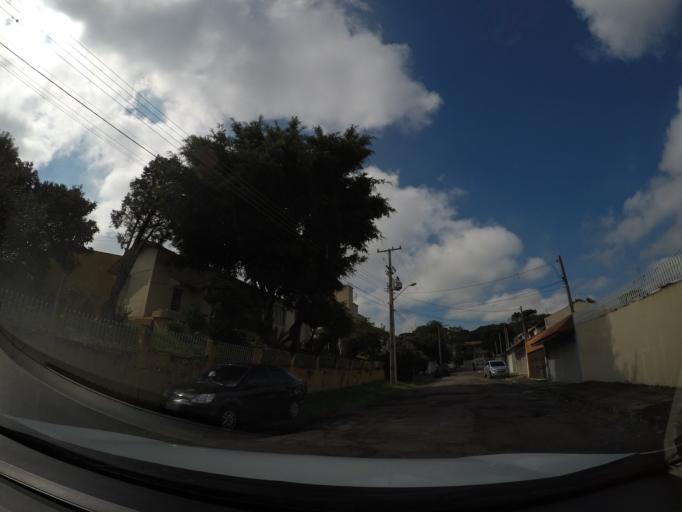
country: BR
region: Parana
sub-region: Sao Jose Dos Pinhais
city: Sao Jose dos Pinhais
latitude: -25.4906
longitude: -49.2195
